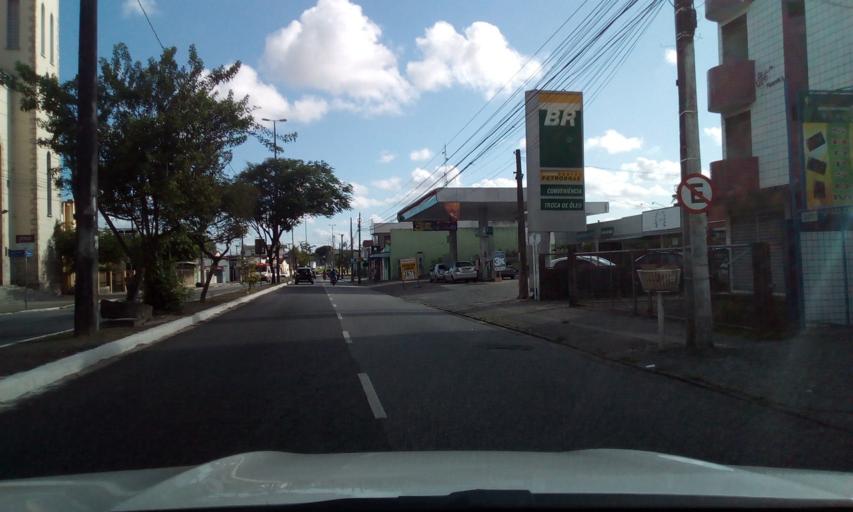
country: BR
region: Paraiba
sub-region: Joao Pessoa
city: Joao Pessoa
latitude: -7.1423
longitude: -34.8903
